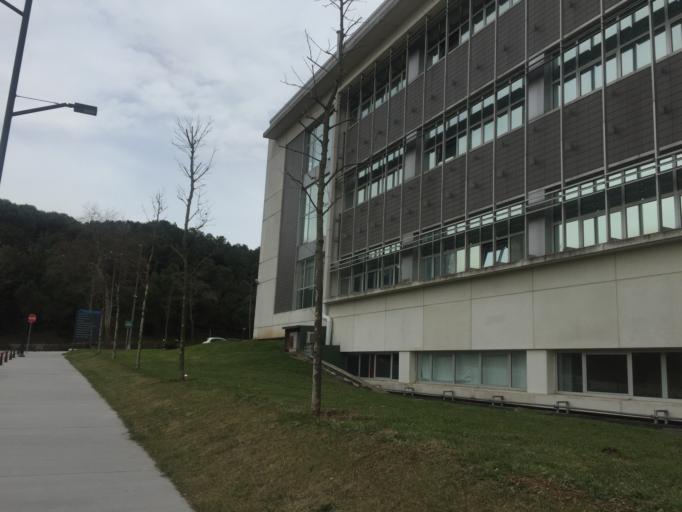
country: TR
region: Istanbul
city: Sisli
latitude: 41.1074
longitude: 29.0276
